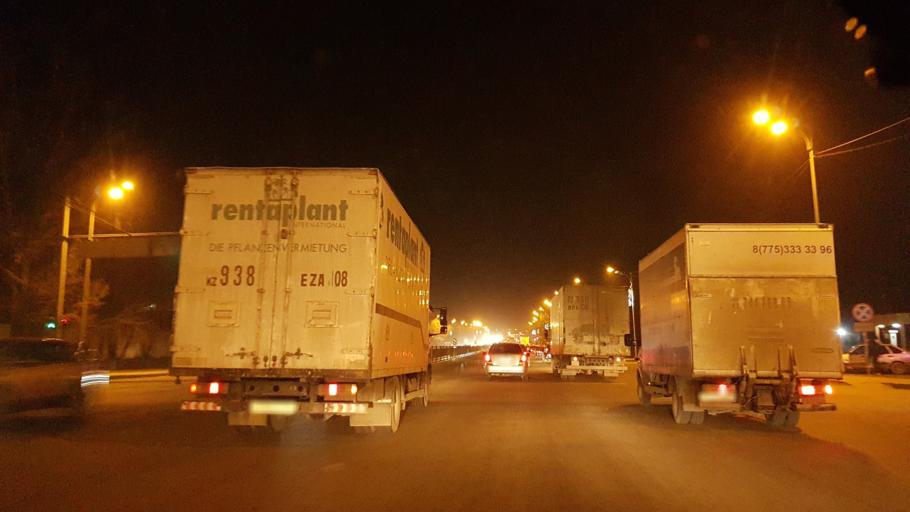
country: KZ
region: Almaty Qalasy
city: Almaty
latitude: 43.2658
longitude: 76.8676
